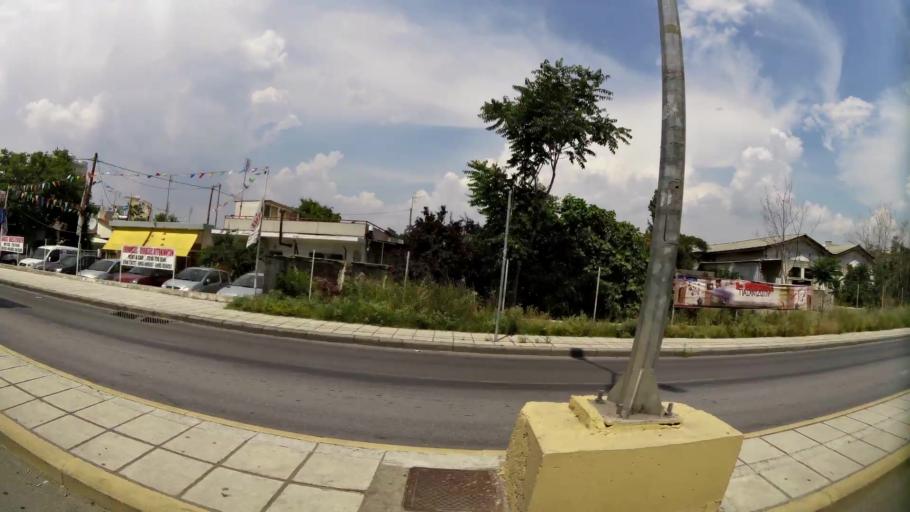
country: GR
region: Central Macedonia
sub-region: Nomos Thessalonikis
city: Stavroupoli
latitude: 40.6649
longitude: 22.9306
